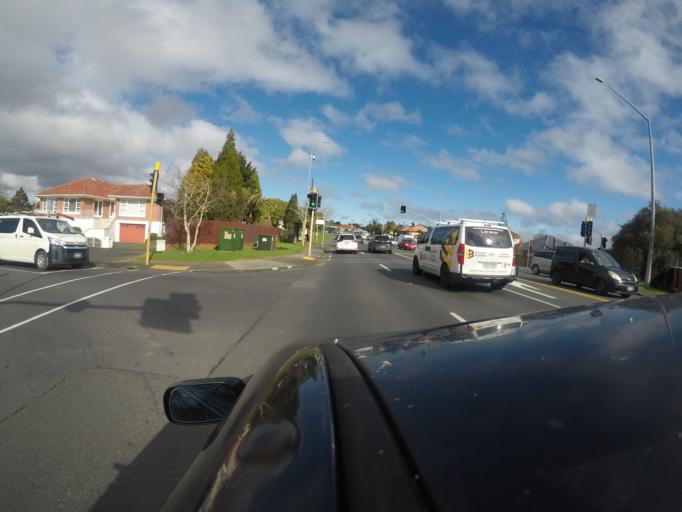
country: NZ
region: Auckland
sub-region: Auckland
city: Waitakere
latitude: -36.8937
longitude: 174.6450
